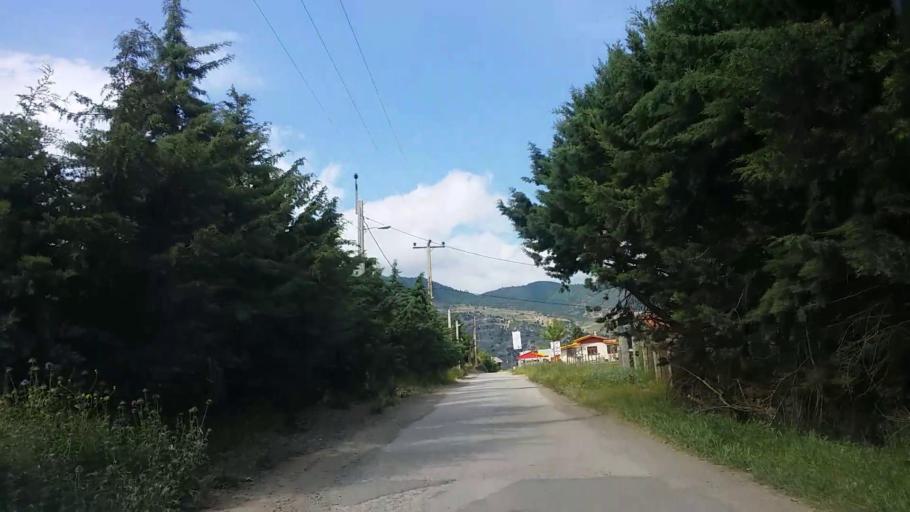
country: IR
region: Mazandaran
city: Chalus
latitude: 36.5343
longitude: 51.2699
